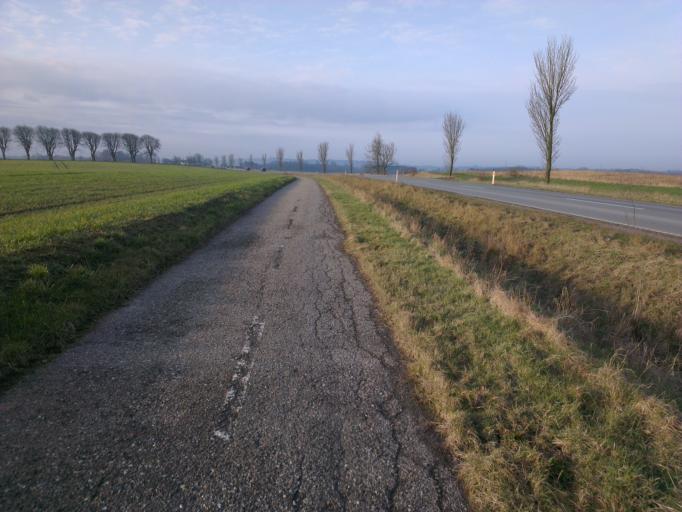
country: DK
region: Capital Region
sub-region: Frederikssund Kommune
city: Jaegerspris
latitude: 55.8210
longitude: 11.9853
